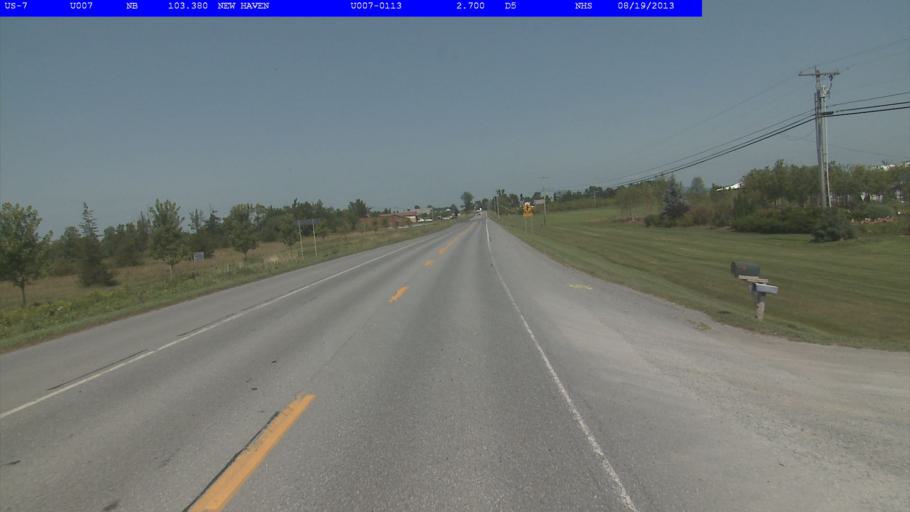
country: US
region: Vermont
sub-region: Addison County
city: Middlebury (village)
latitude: 44.0844
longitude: -73.1763
